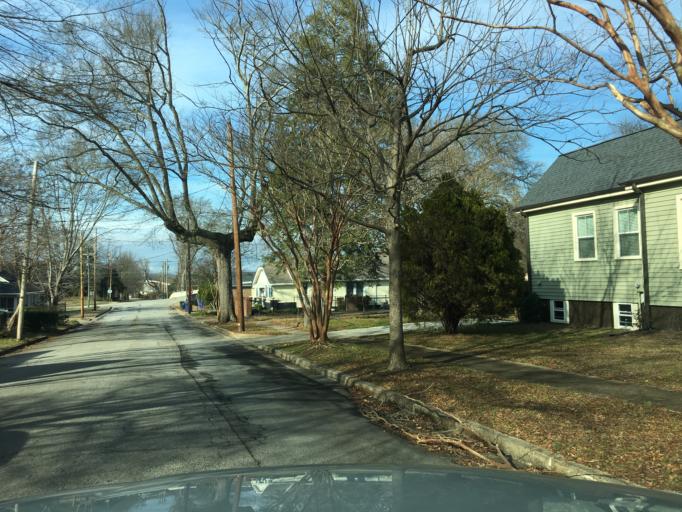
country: US
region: South Carolina
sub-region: Greenville County
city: Greenville
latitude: 34.8625
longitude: -82.4108
